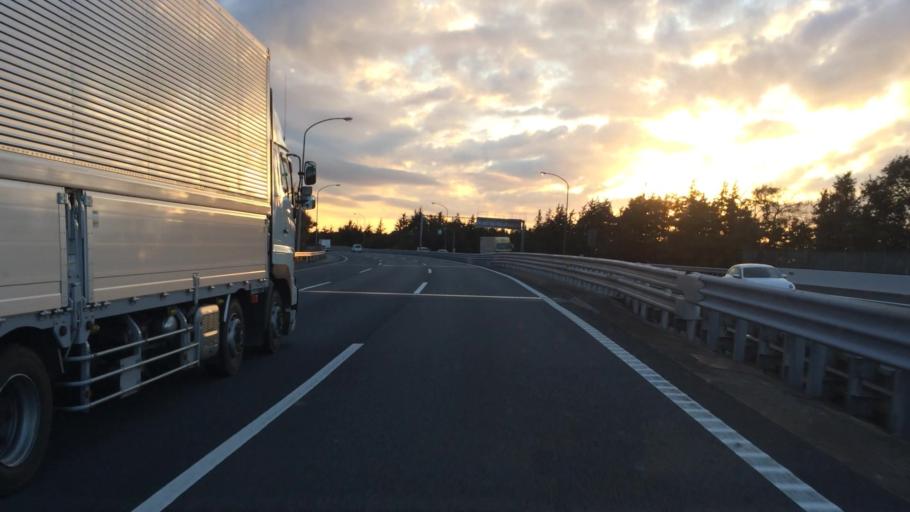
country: JP
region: Chiba
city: Chiba
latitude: 35.6634
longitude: 140.1028
